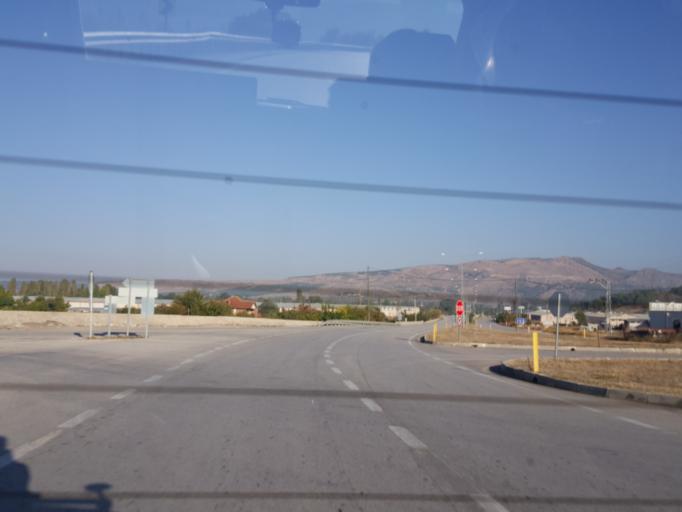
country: TR
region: Amasya
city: Amasya
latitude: 40.5591
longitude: 35.7931
